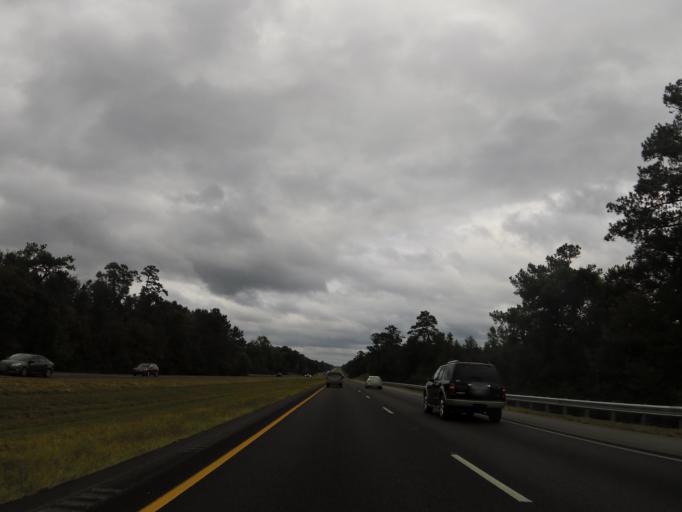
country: US
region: Alabama
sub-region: Conecuh County
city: Evergreen
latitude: 31.3864
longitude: -87.0345
